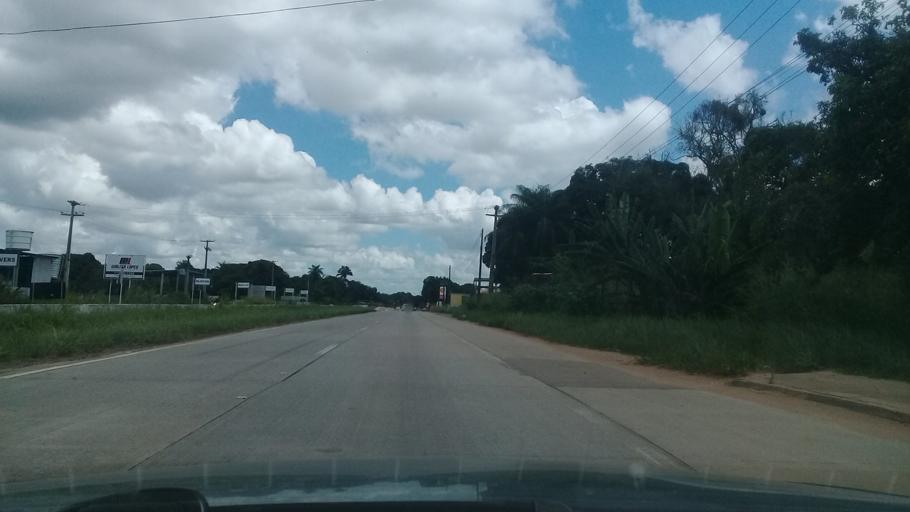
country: BR
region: Pernambuco
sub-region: Sao Lourenco Da Mata
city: Sao Lourenco da Mata
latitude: -7.9334
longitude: -35.1322
